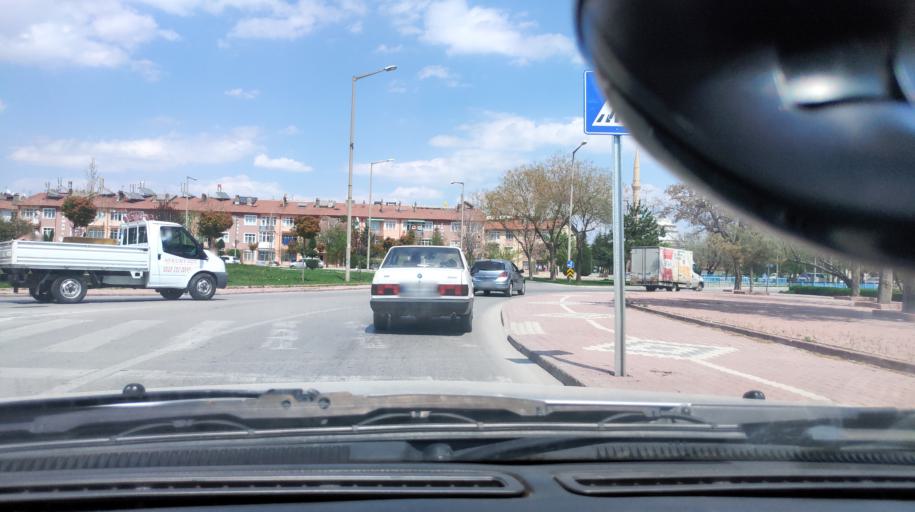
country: TR
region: Konya
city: Selcuklu
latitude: 37.9291
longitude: 32.5030
